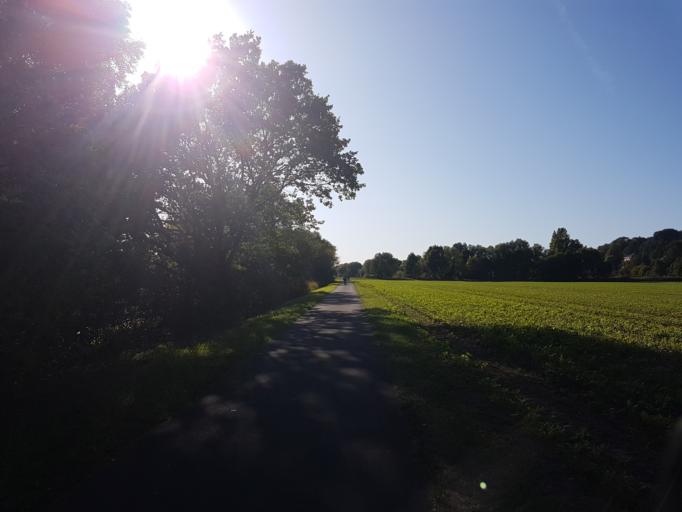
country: DE
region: North Rhine-Westphalia
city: Porta Westfalica
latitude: 52.2403
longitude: 8.8994
